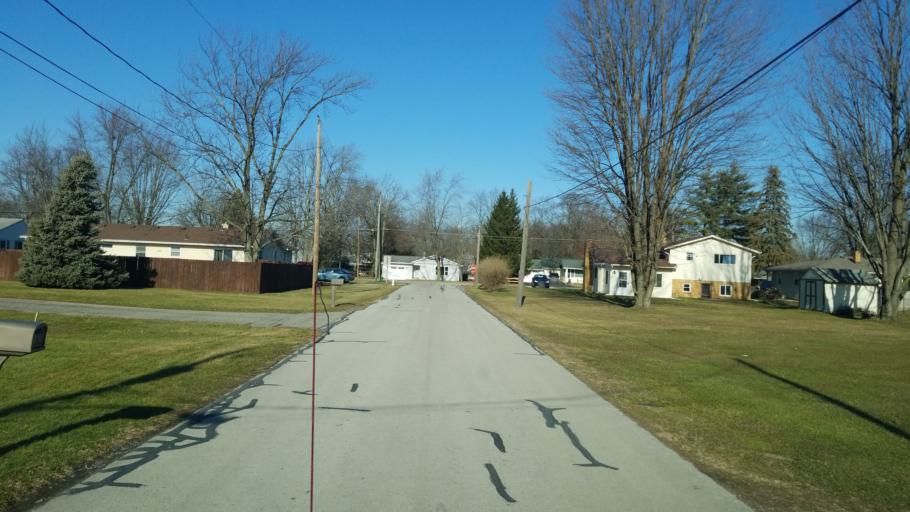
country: US
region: Ohio
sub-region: Wood County
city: Weston
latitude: 41.4104
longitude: -83.8585
